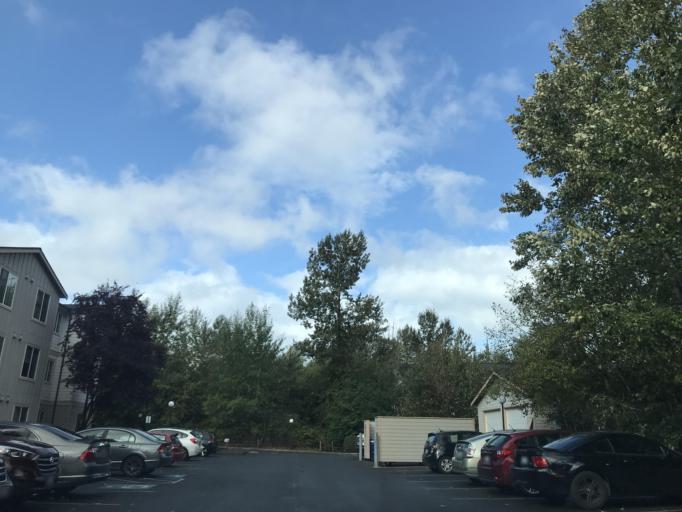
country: US
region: Washington
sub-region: Whatcom County
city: Bellingham
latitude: 48.7884
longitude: -122.5018
